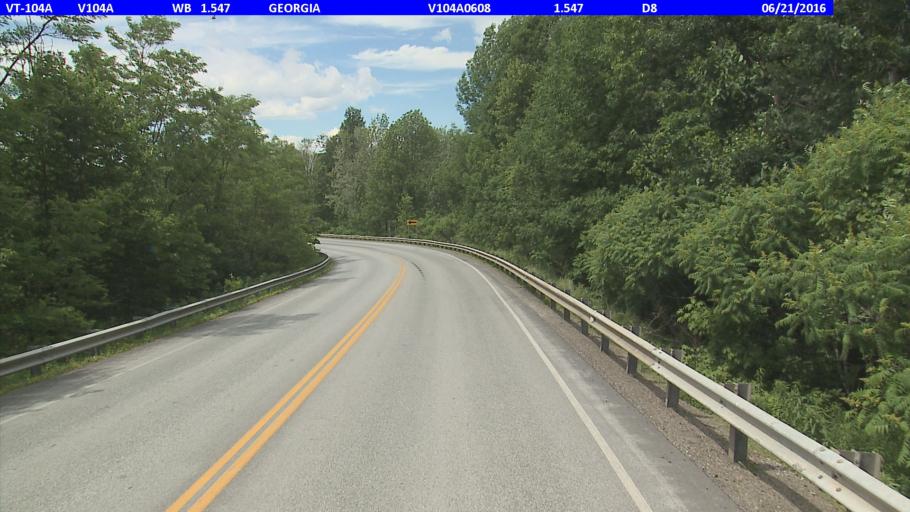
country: US
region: Vermont
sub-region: Chittenden County
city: Milton
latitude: 44.6814
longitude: -73.0850
